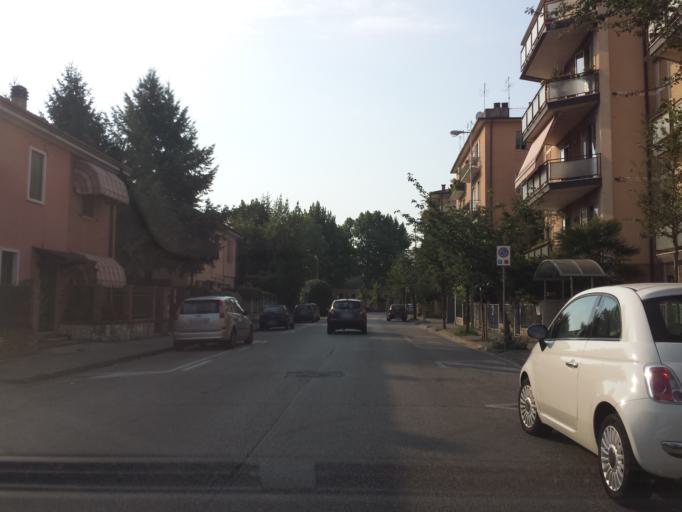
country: IT
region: Veneto
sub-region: Provincia di Vicenza
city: Vicenza
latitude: 45.5634
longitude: 11.5401
